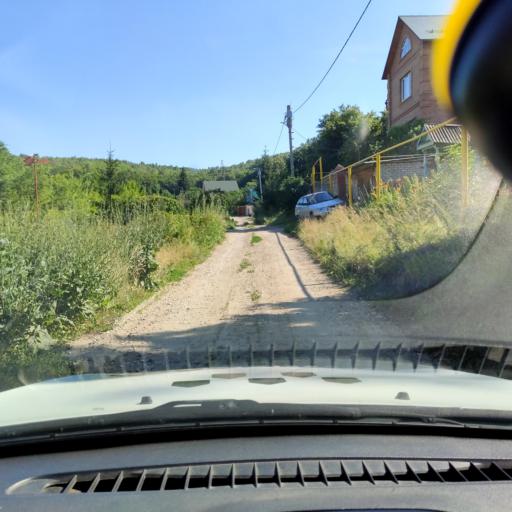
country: RU
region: Samara
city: Zhigulevsk
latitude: 53.3944
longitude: 49.5296
